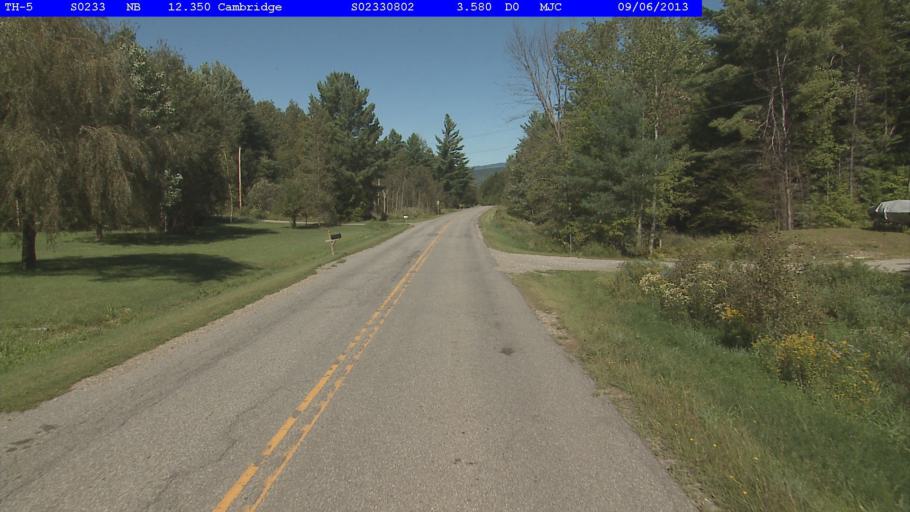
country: US
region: Vermont
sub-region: Lamoille County
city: Johnson
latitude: 44.6309
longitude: -72.8462
